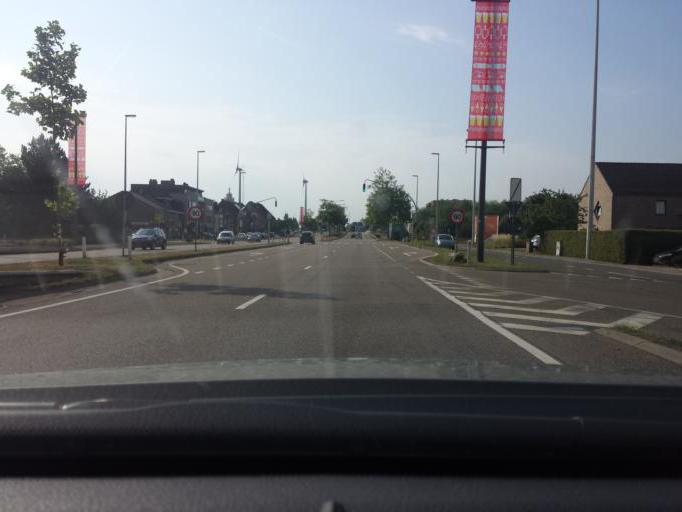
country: BE
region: Flanders
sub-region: Provincie Limburg
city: Hasselt
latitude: 50.9204
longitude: 5.3221
